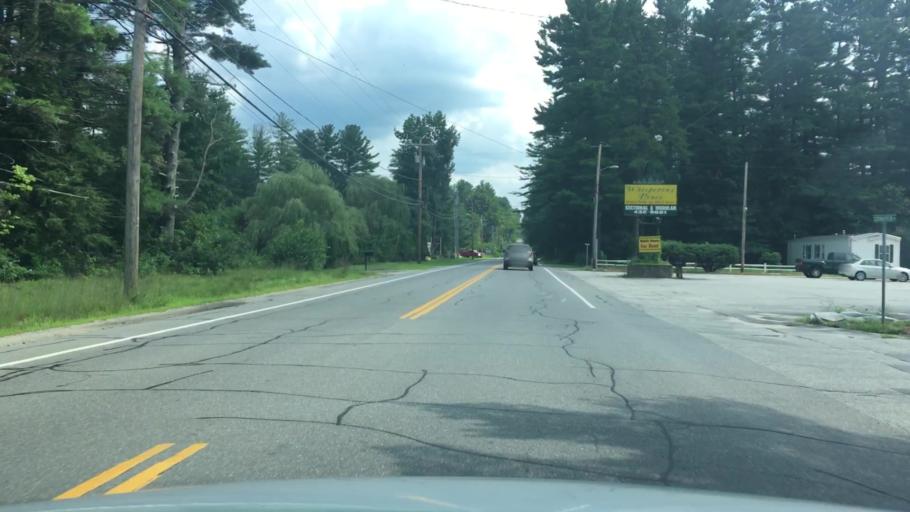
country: US
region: New Hampshire
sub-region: Rockingham County
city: Derry Village
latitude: 42.9398
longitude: -71.3453
